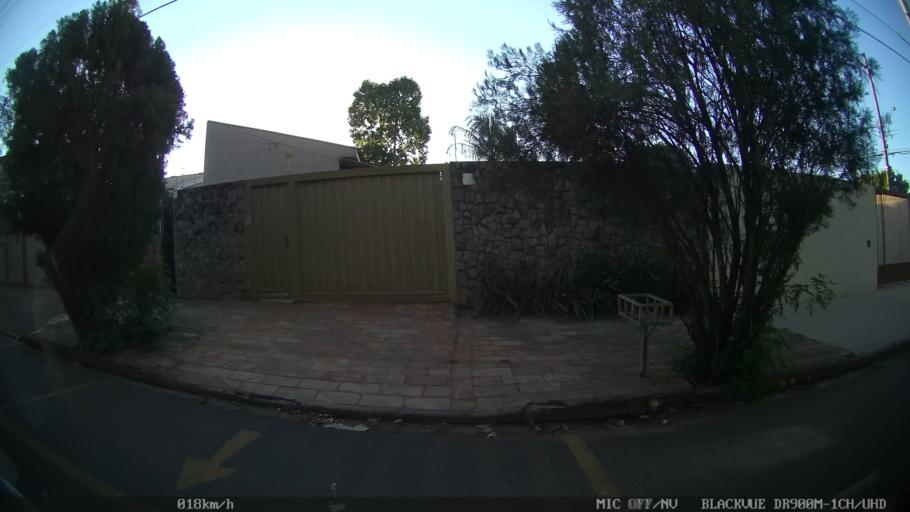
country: BR
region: Sao Paulo
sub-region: Sao Jose Do Rio Preto
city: Sao Jose do Rio Preto
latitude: -20.7782
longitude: -49.3569
